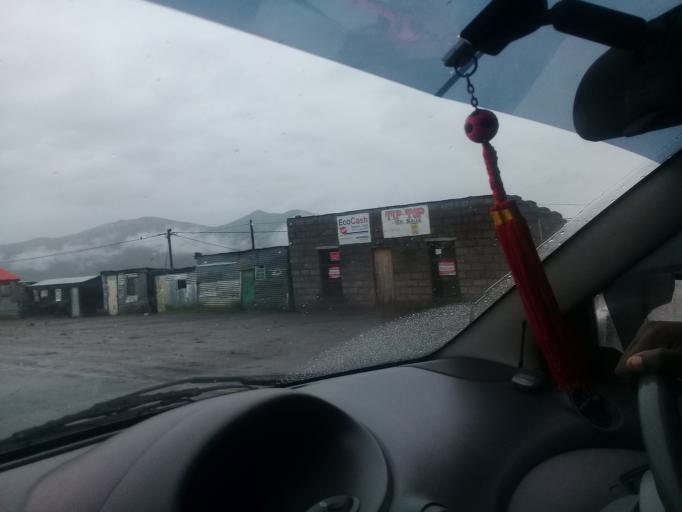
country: LS
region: Mokhotlong
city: Mokhotlong
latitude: -29.3000
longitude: 29.0329
